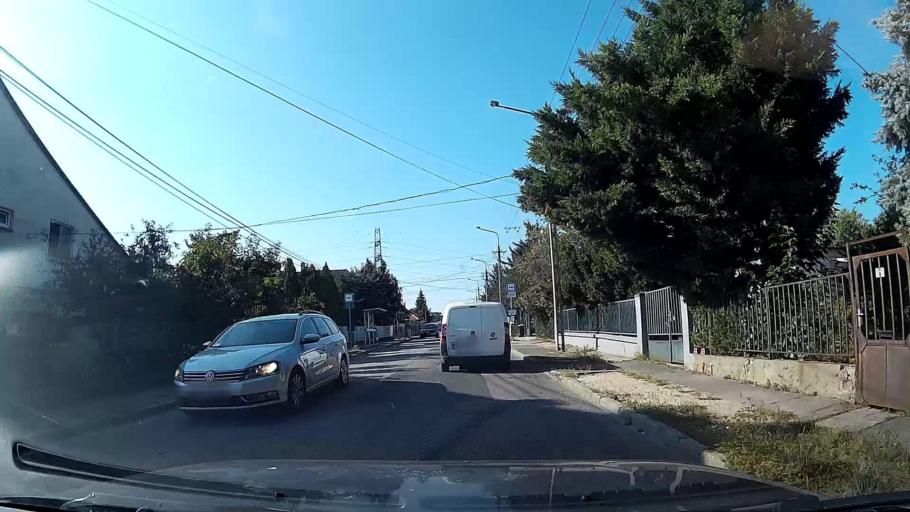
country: HU
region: Budapest
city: Budapest XXII. keruelet
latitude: 47.4243
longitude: 19.0028
